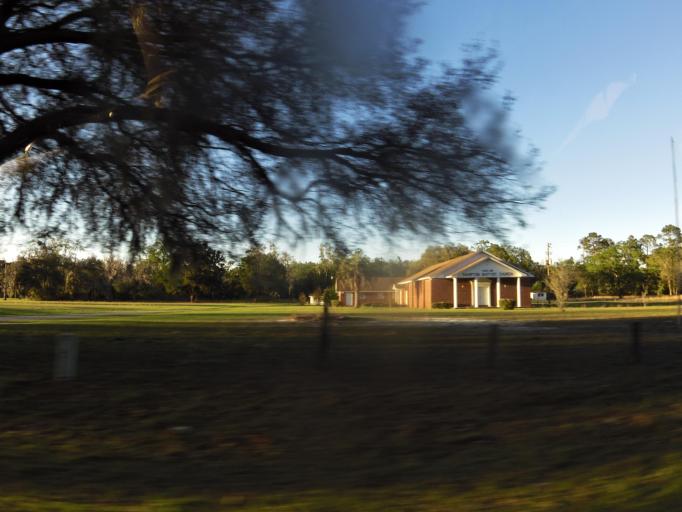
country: US
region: Florida
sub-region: Alachua County
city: Waldo
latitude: 29.8643
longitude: -82.1458
